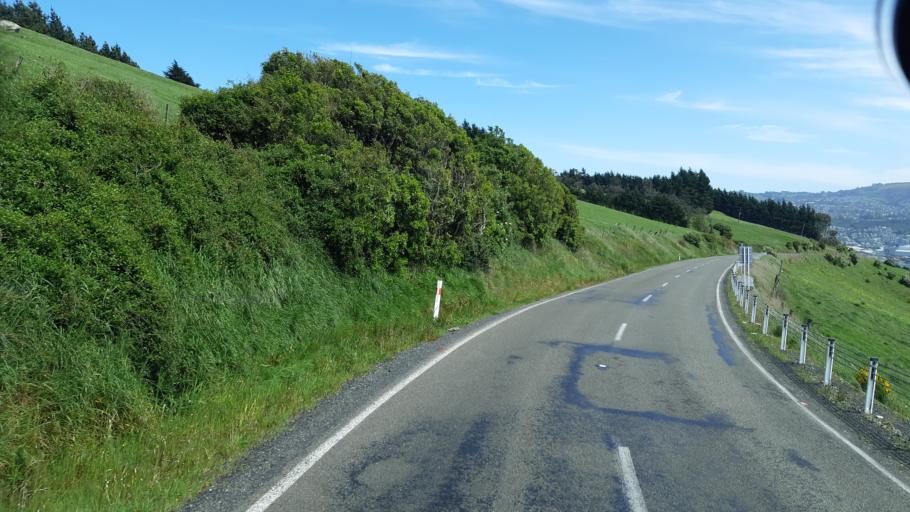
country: NZ
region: Otago
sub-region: Dunedin City
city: Dunedin
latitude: -45.8853
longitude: 170.5636
